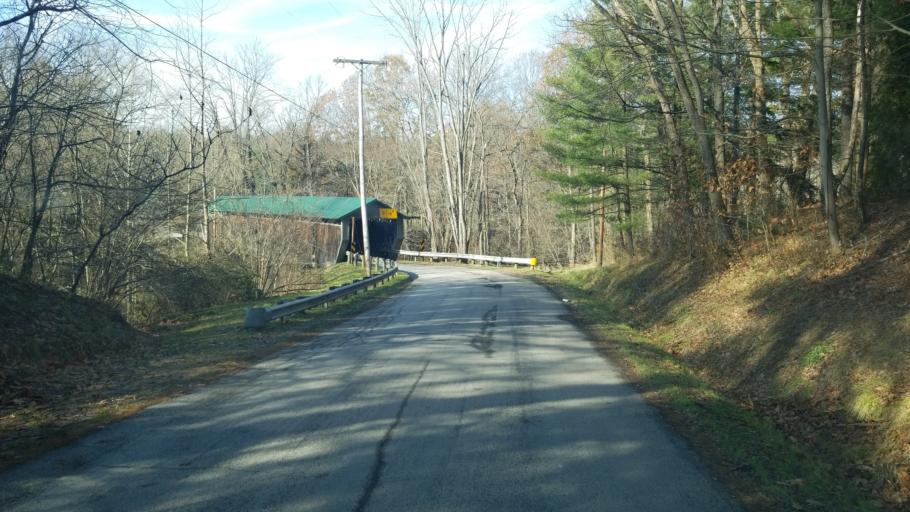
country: US
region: Ohio
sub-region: Ashtabula County
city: Roaming Shores
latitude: 41.6731
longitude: -80.8707
